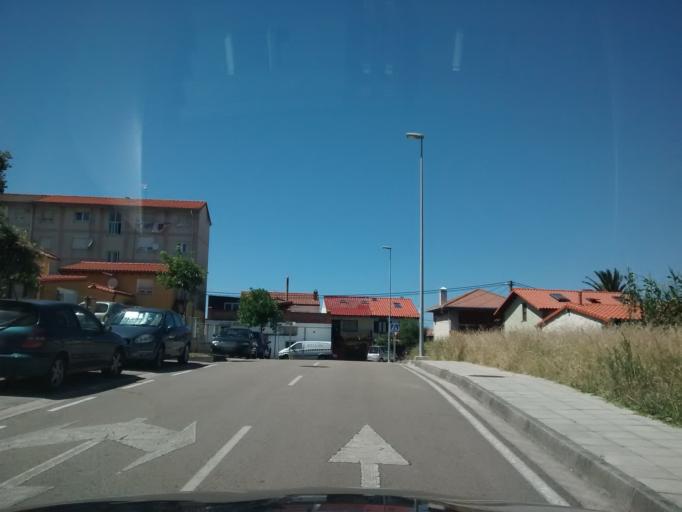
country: ES
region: Cantabria
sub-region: Provincia de Cantabria
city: Santander
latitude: 43.4817
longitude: -3.8009
